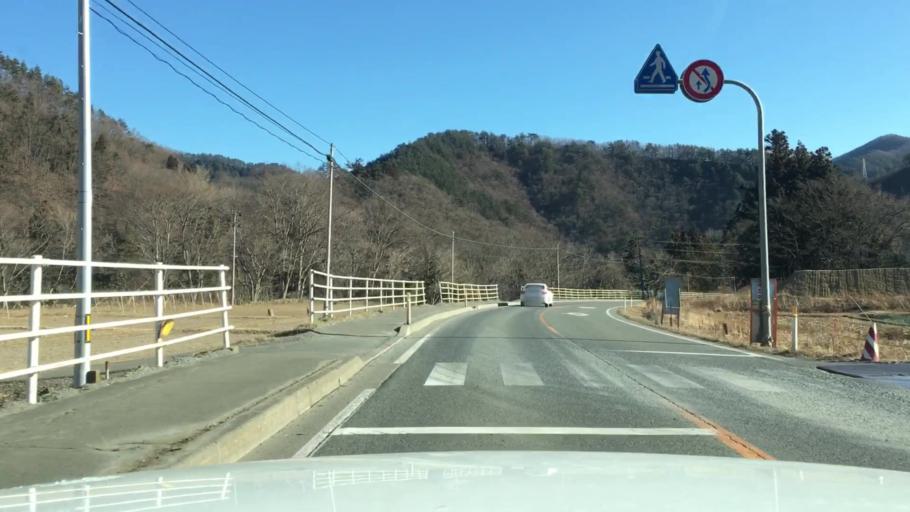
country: JP
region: Iwate
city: Miyako
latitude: 39.6028
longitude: 141.7658
